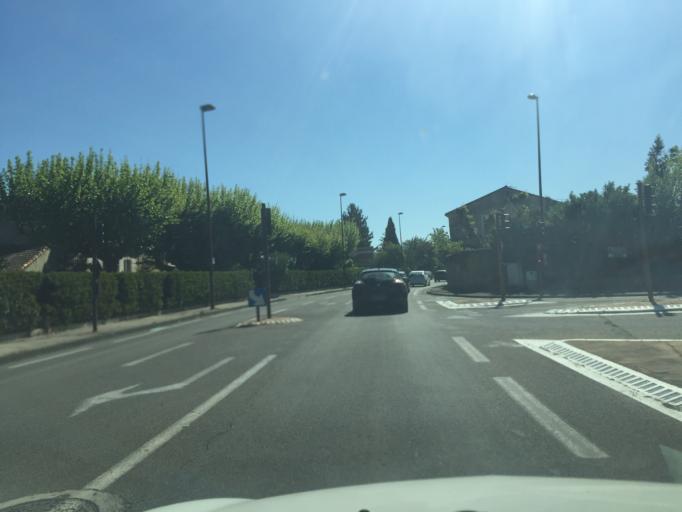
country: FR
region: Provence-Alpes-Cote d'Azur
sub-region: Departement du Vaucluse
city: Le Pontet
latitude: 43.9523
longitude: 4.8441
